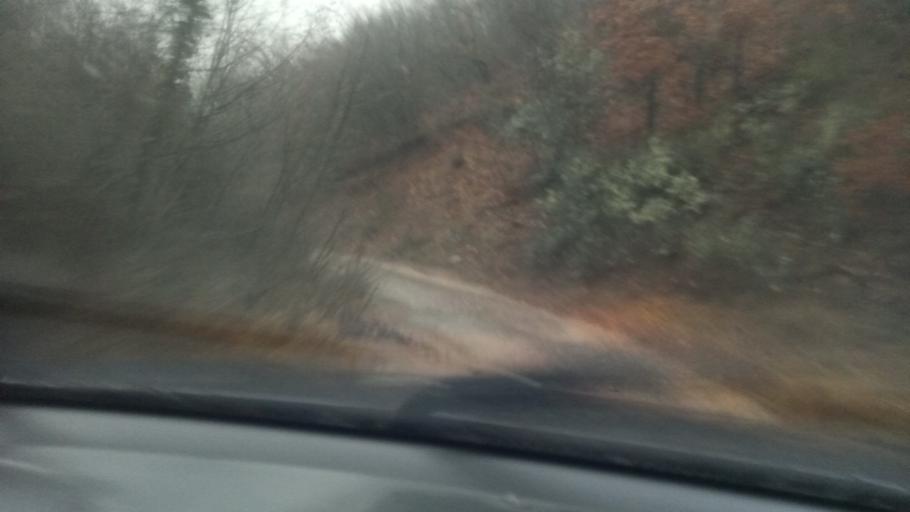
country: MK
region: Vinica
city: Blatec
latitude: 41.8332
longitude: 22.6063
